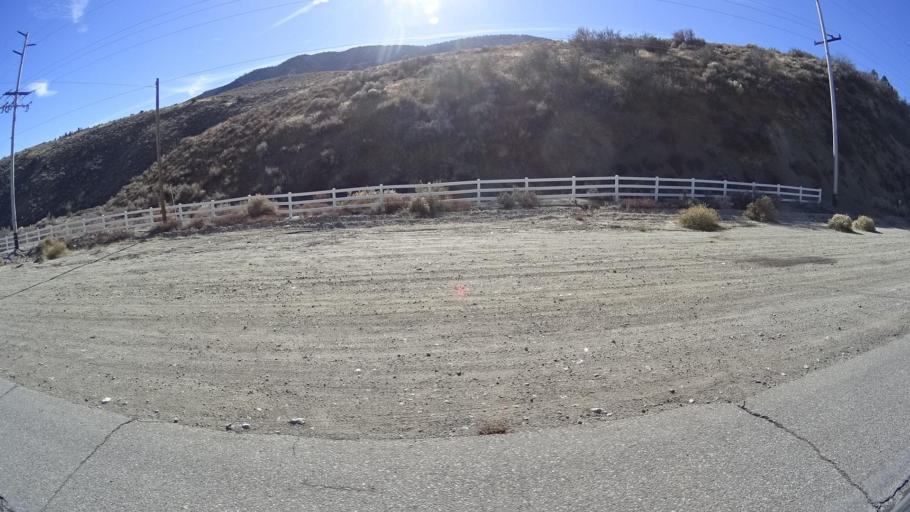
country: US
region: California
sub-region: Kern County
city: Frazier Park
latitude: 34.8203
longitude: -118.9194
